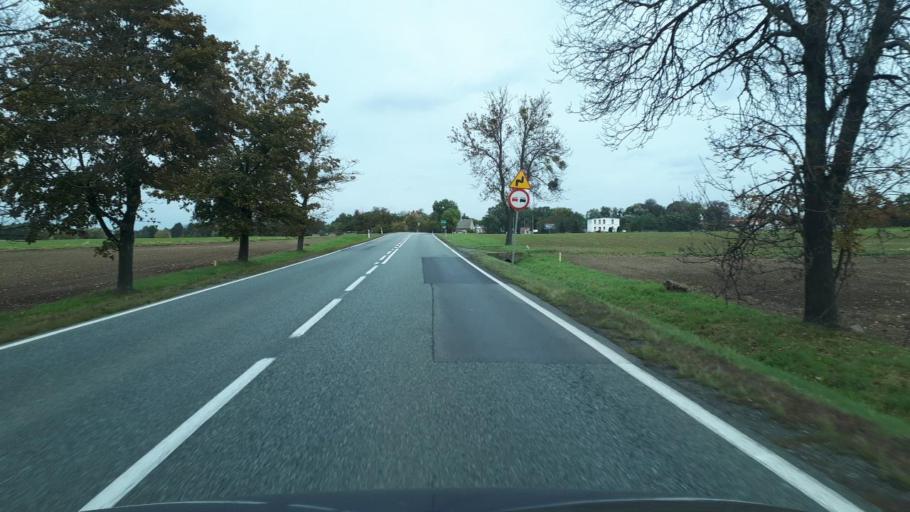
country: PL
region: Opole Voivodeship
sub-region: Powiat kluczborski
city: Byczyna
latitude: 51.0580
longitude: 18.1987
